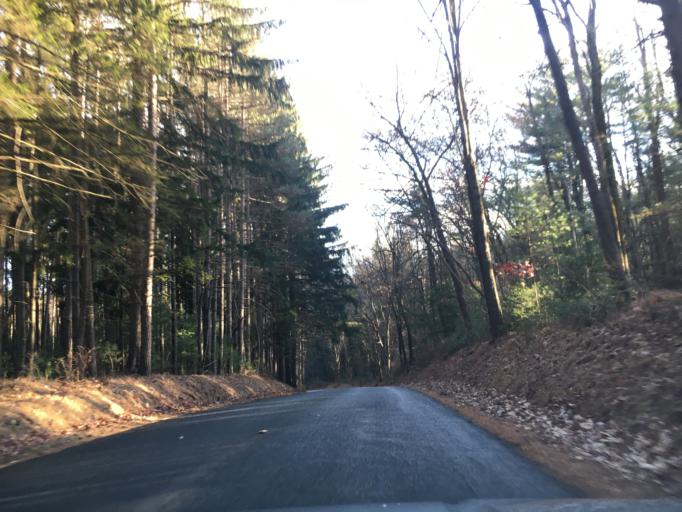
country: US
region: Pennsylvania
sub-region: Carbon County
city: Lehighton
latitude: 40.7920
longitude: -75.7193
